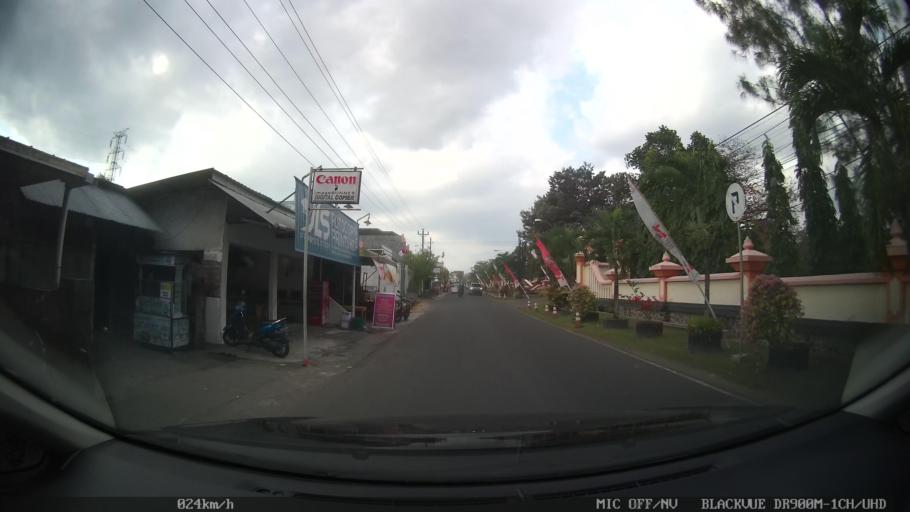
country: ID
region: Daerah Istimewa Yogyakarta
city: Yogyakarta
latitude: -7.7836
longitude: 110.3420
